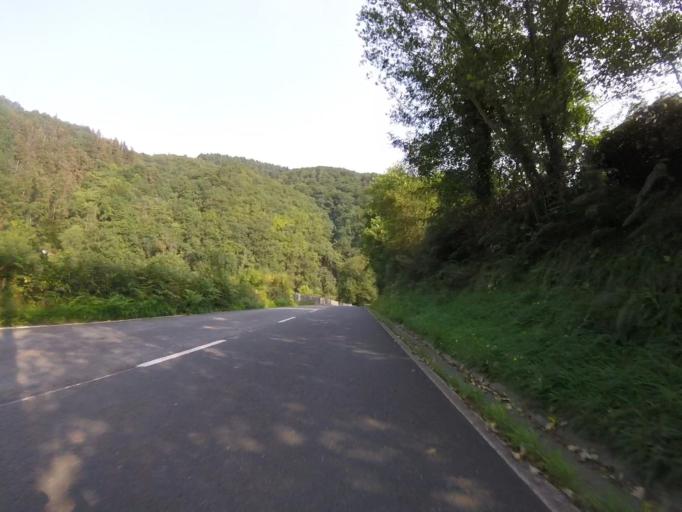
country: ES
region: Navarre
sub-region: Provincia de Navarra
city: Arano
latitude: 43.2193
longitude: -1.9053
